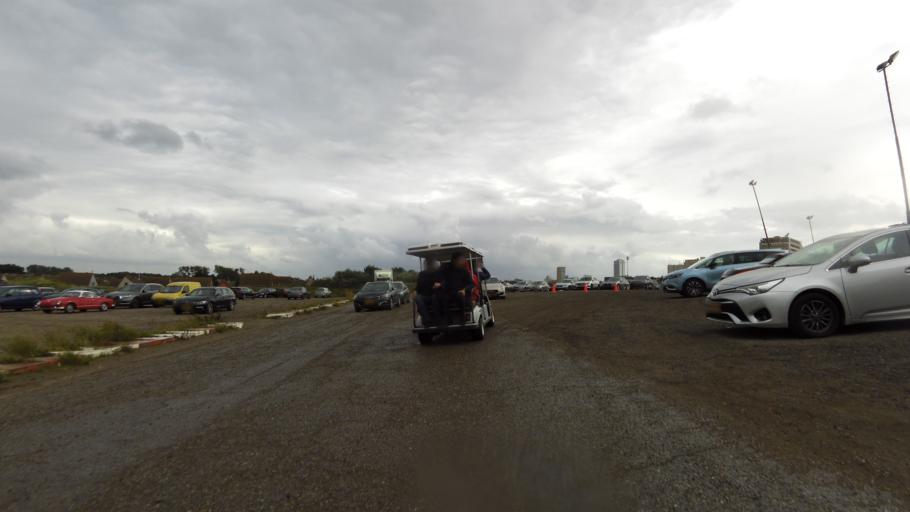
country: NL
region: North Holland
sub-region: Gemeente Zandvoort
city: Zandvoort
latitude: 52.3844
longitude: 4.5378
